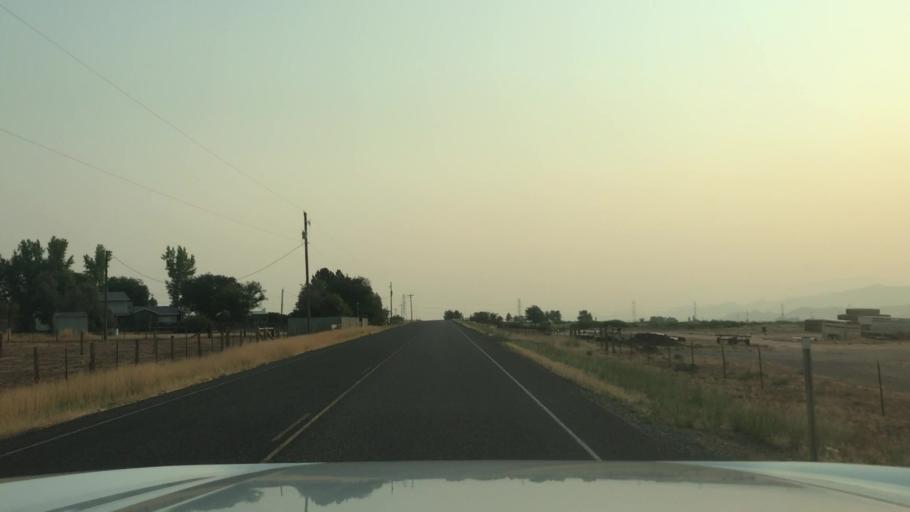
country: US
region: Utah
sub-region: Sevier County
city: Aurora
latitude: 38.8887
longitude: -111.9557
